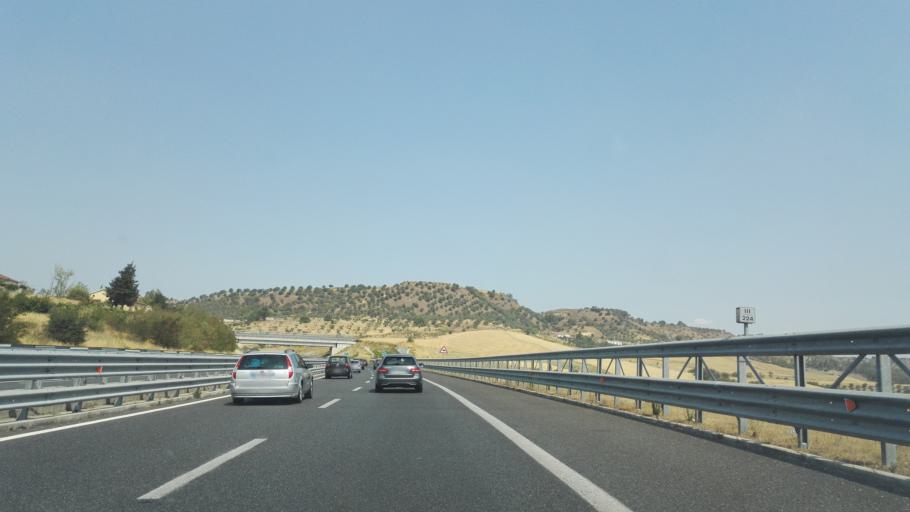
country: IT
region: Calabria
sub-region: Provincia di Cosenza
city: Tarsia
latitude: 39.5944
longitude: 16.2452
